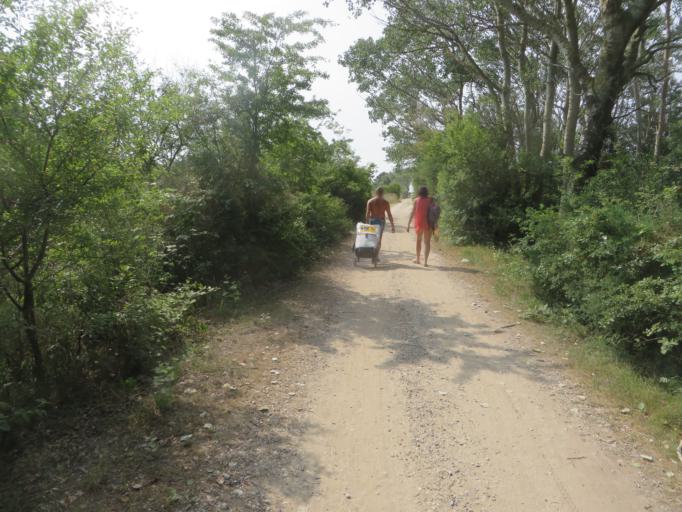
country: IT
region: Veneto
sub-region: Provincia di Venezia
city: Crepaldo
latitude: 45.5343
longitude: 12.7338
